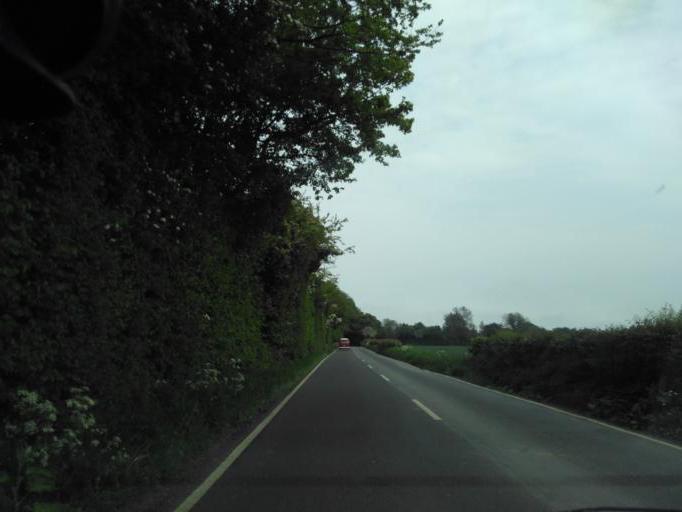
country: GB
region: England
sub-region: Kent
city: Lyminge
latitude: 51.1895
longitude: 1.0549
